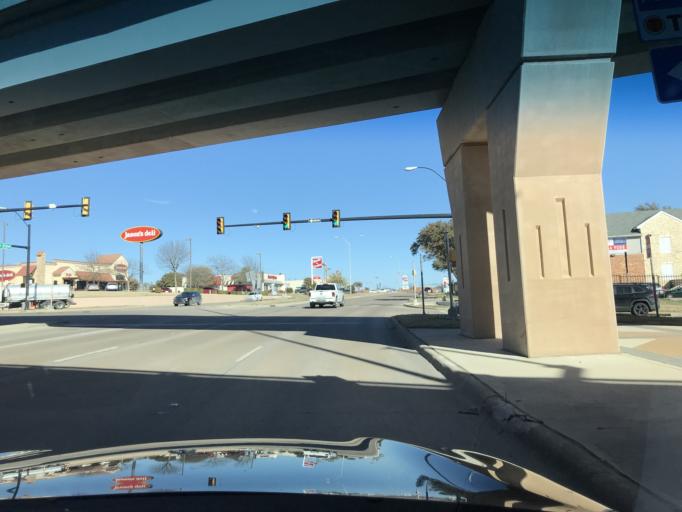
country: US
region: Texas
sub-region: Tarrant County
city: Benbrook
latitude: 32.6765
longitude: -97.4066
